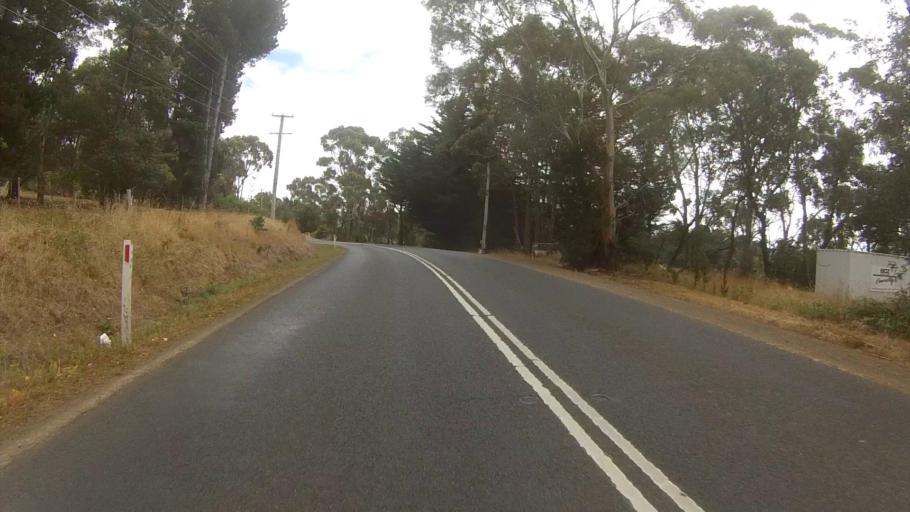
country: AU
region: Tasmania
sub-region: Kingborough
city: Margate
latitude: -43.0196
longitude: 147.2536
